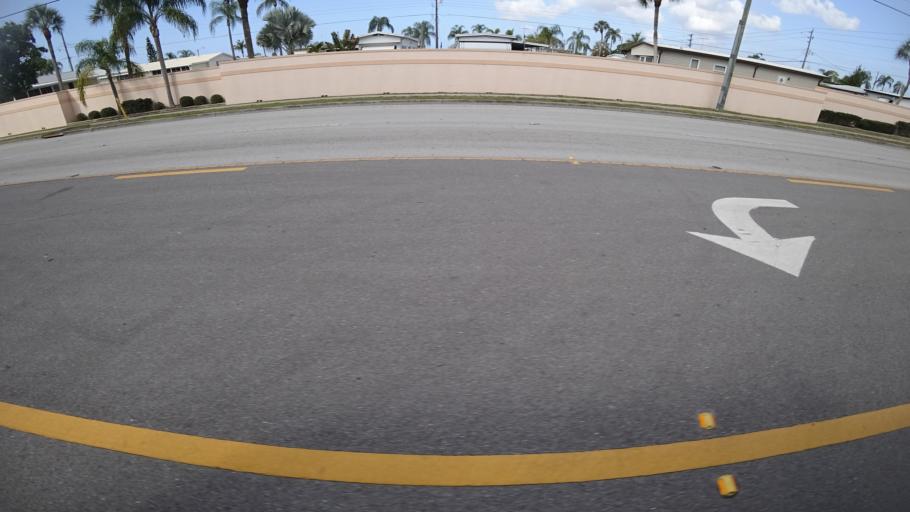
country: US
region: Florida
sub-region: Manatee County
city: West Samoset
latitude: 27.4538
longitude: -82.5548
